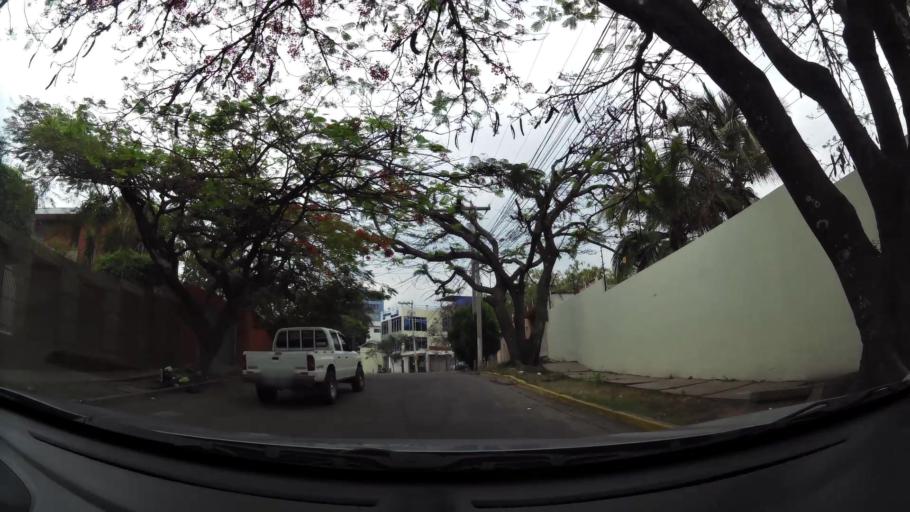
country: HN
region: Francisco Morazan
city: Tegucigalpa
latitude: 14.1034
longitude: -87.1926
